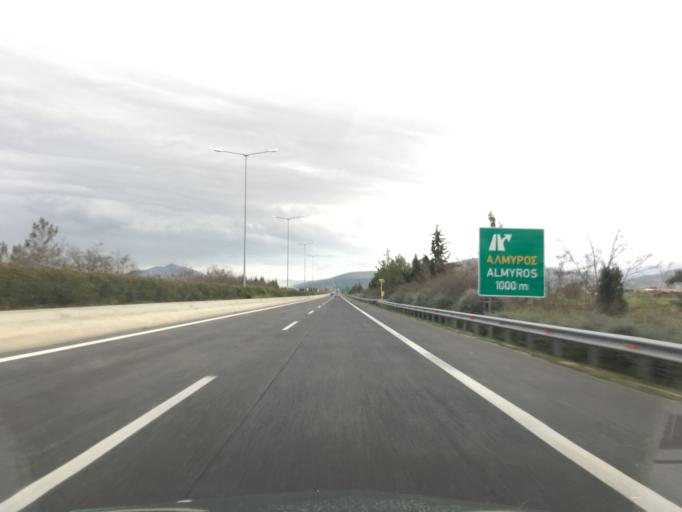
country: GR
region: Thessaly
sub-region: Nomos Magnisias
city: Almyros
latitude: 39.2040
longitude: 22.7590
